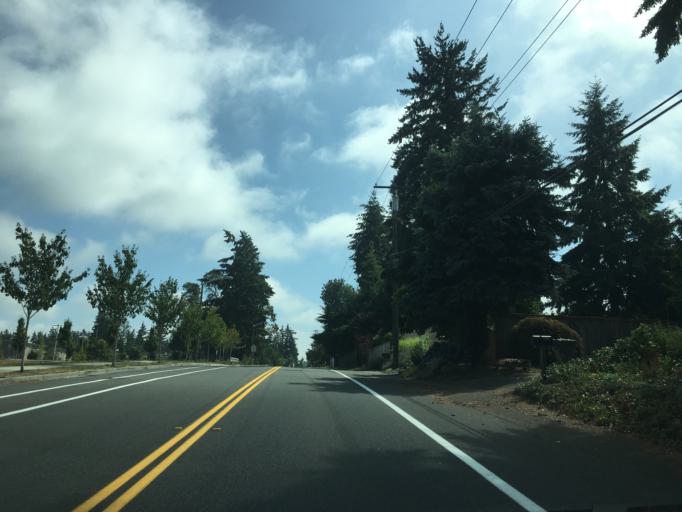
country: US
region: Washington
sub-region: King County
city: Inglewood-Finn Hill
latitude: 47.7188
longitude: -122.2334
